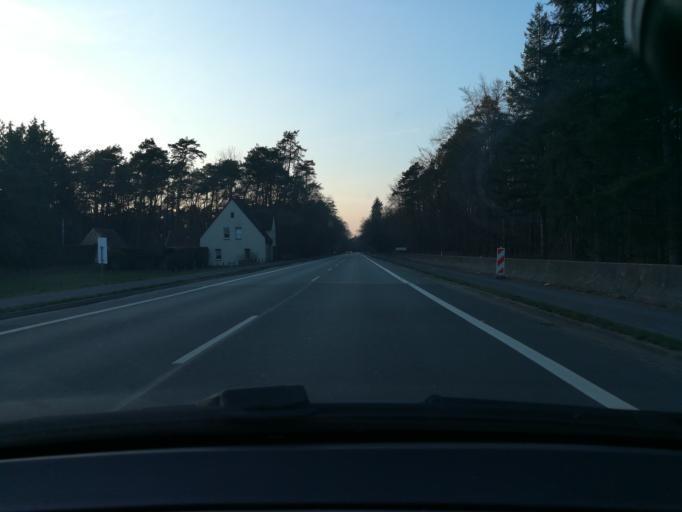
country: DE
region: North Rhine-Westphalia
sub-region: Regierungsbezirk Detmold
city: Oerlinghausen
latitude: 51.9370
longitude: 8.5953
